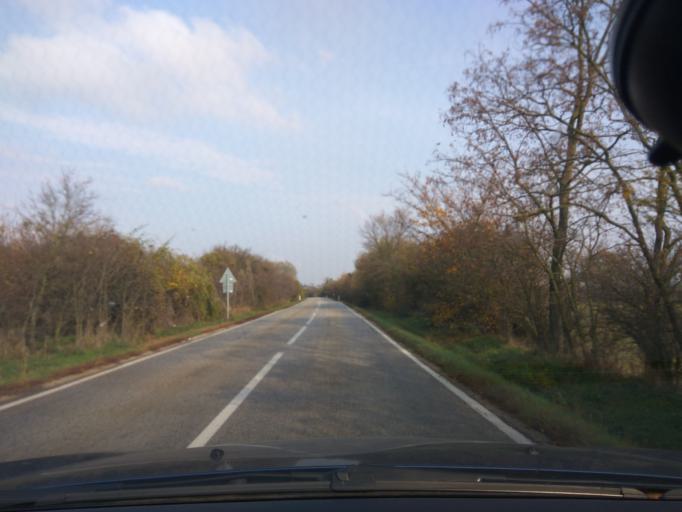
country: SK
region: Trnavsky
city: Vrbove
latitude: 48.6518
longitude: 17.7539
